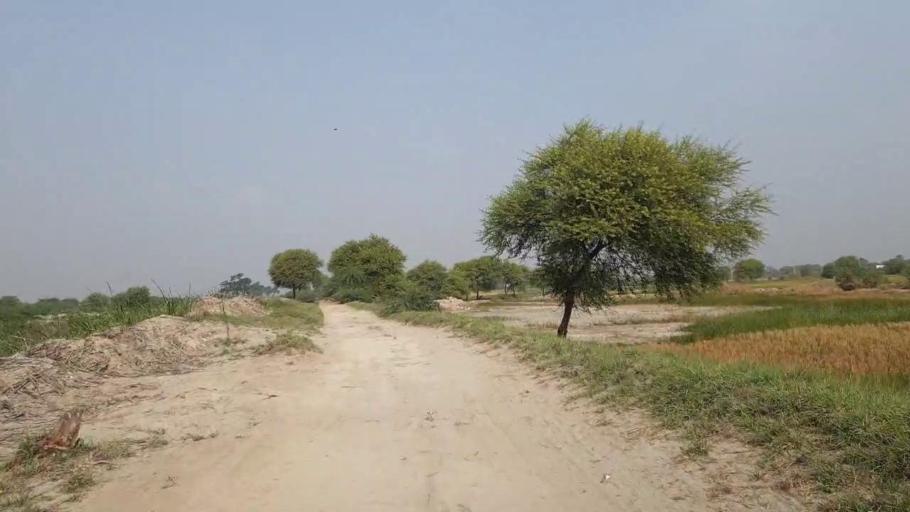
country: PK
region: Sindh
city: Kario
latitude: 24.7679
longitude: 68.5235
